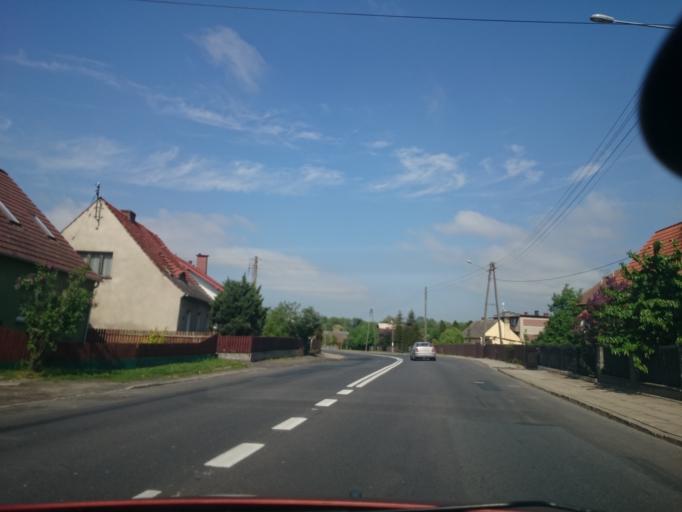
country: PL
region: Opole Voivodeship
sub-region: Powiat opolski
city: Dabrowa
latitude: 50.7202
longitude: 17.7682
